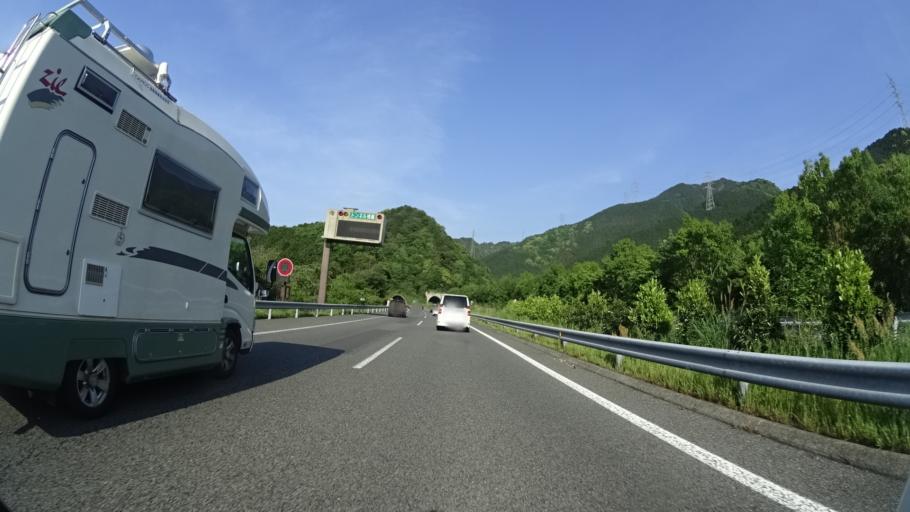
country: JP
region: Ehime
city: Saijo
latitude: 33.8846
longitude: 133.1863
